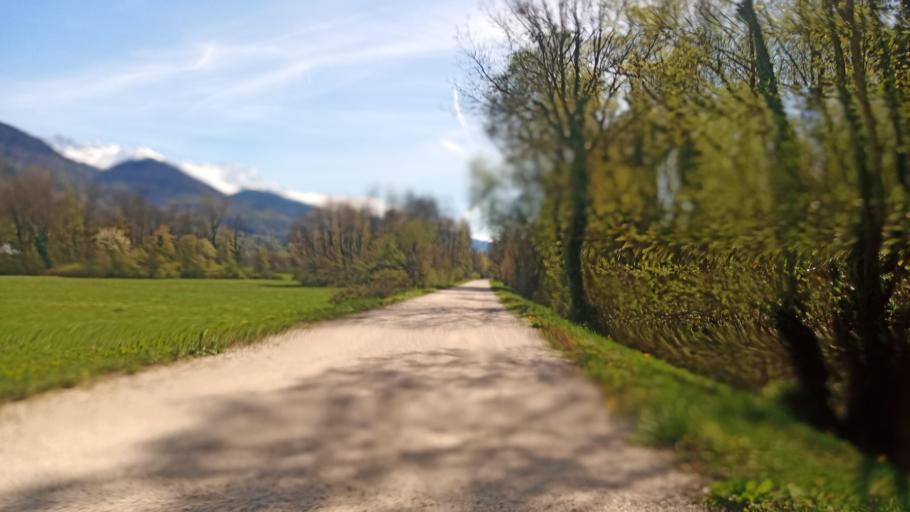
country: FR
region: Rhone-Alpes
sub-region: Departement de l'Isere
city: Goncelin
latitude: 45.3376
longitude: 5.9671
